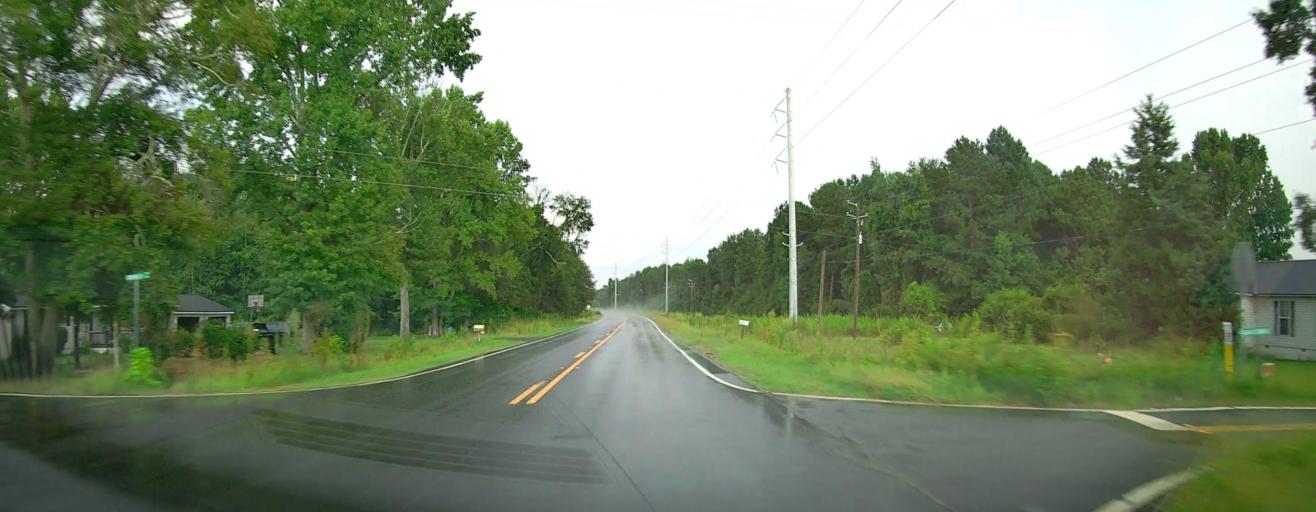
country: US
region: Georgia
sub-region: Twiggs County
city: Jeffersonville
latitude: 32.5749
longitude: -83.2015
